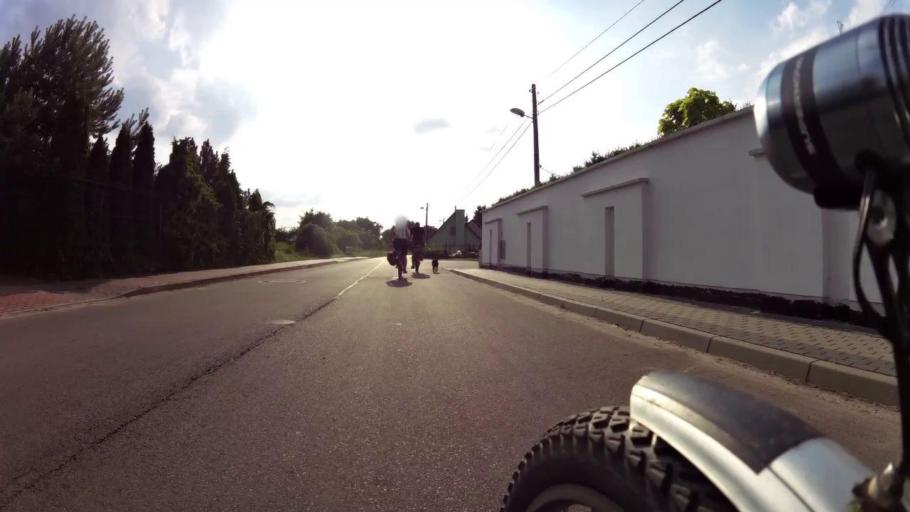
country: PL
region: West Pomeranian Voivodeship
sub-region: Powiat goleniowski
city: Stepnica
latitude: 53.6563
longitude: 14.5236
